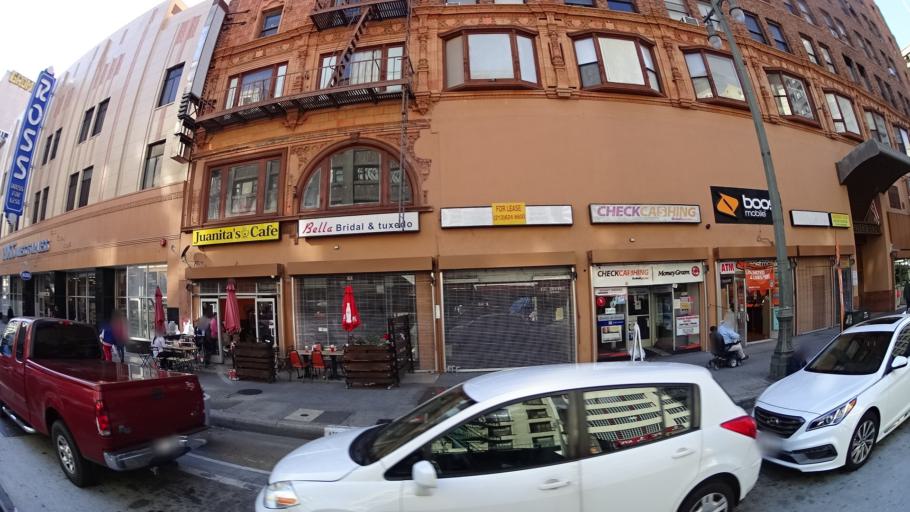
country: US
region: California
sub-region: Los Angeles County
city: Los Angeles
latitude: 34.0450
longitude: -118.2541
